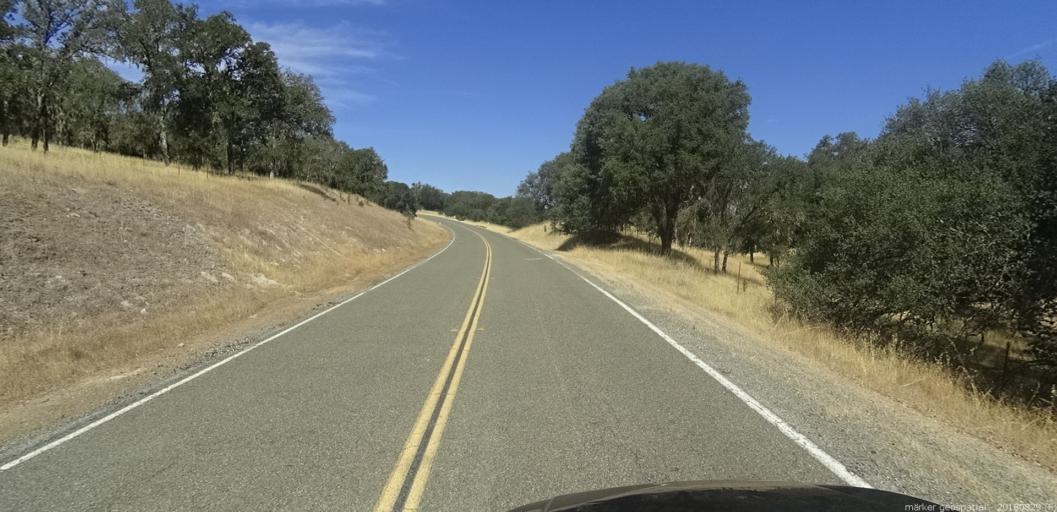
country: US
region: California
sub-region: San Luis Obispo County
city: Lake Nacimiento
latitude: 35.8074
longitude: -120.9954
